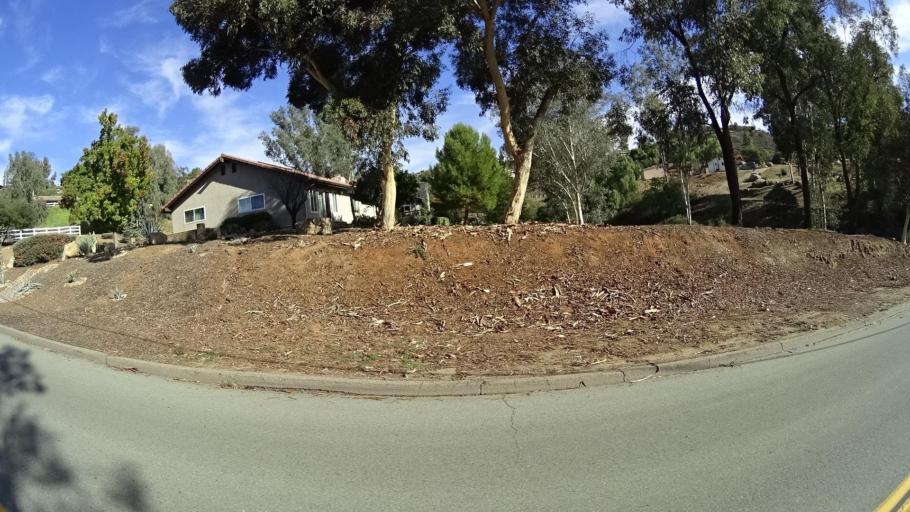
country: US
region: California
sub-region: San Diego County
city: Alpine
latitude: 32.8176
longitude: -116.7434
